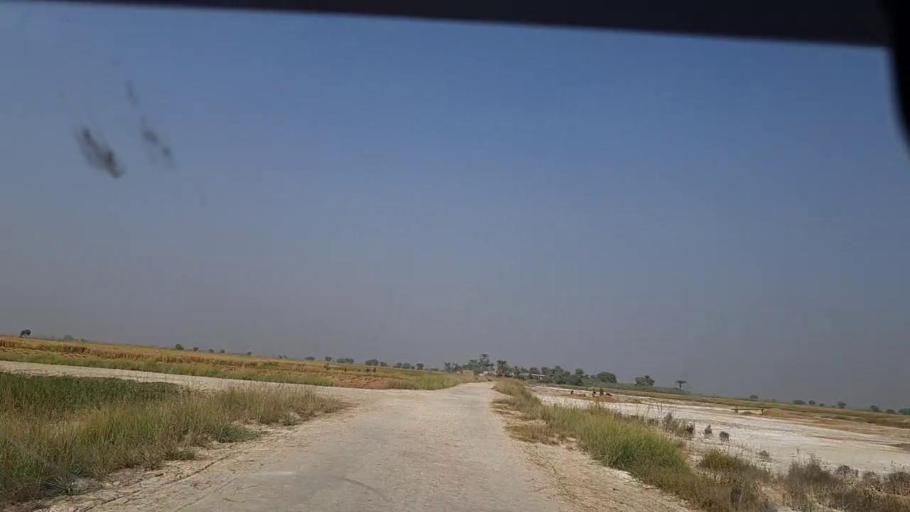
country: PK
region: Sindh
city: Shikarpur
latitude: 28.0918
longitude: 68.5993
